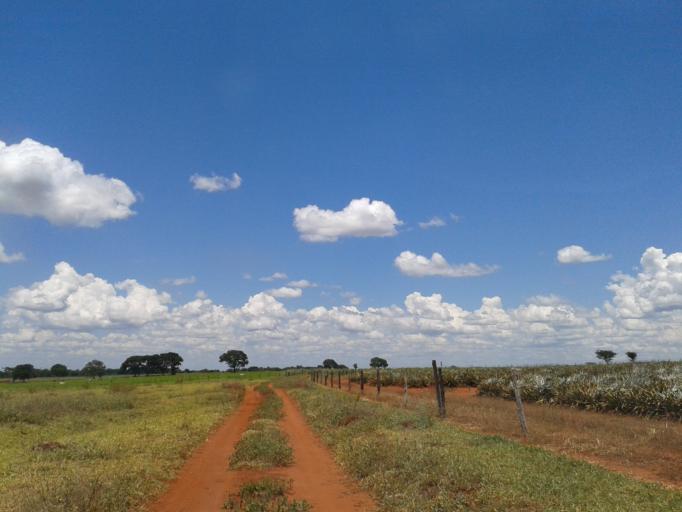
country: BR
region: Minas Gerais
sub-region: Centralina
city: Centralina
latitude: -18.6993
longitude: -49.1638
